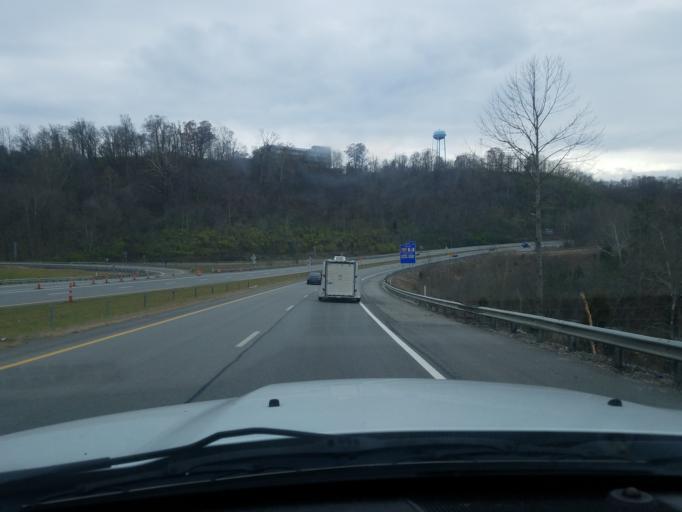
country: US
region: West Virginia
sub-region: Cabell County
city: Huntington
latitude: 38.3940
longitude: -82.4532
